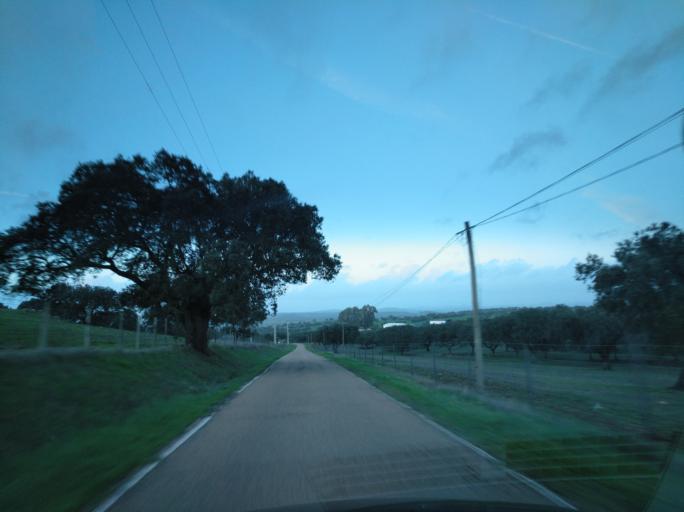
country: PT
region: Portalegre
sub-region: Campo Maior
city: Campo Maior
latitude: 39.0716
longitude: -7.1155
